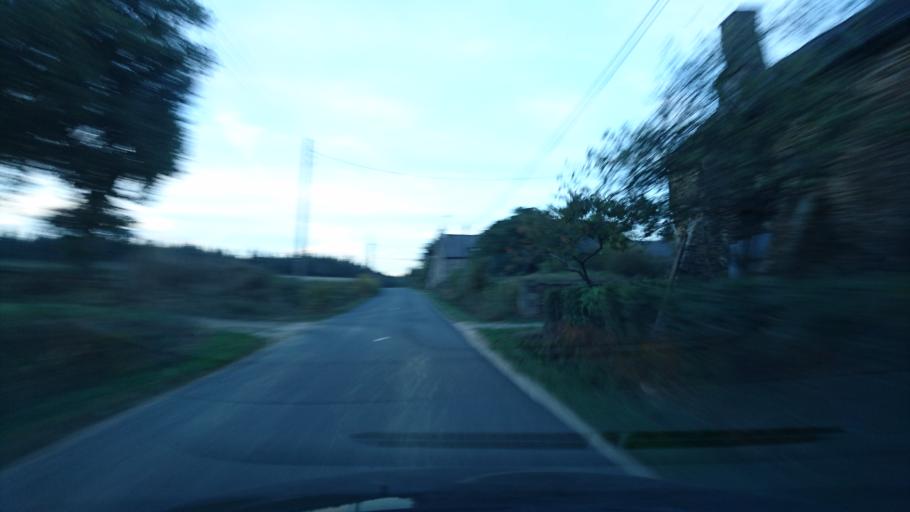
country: FR
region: Brittany
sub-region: Departement d'Ille-et-Vilaine
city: Guignen
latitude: 47.8834
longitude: -1.8924
